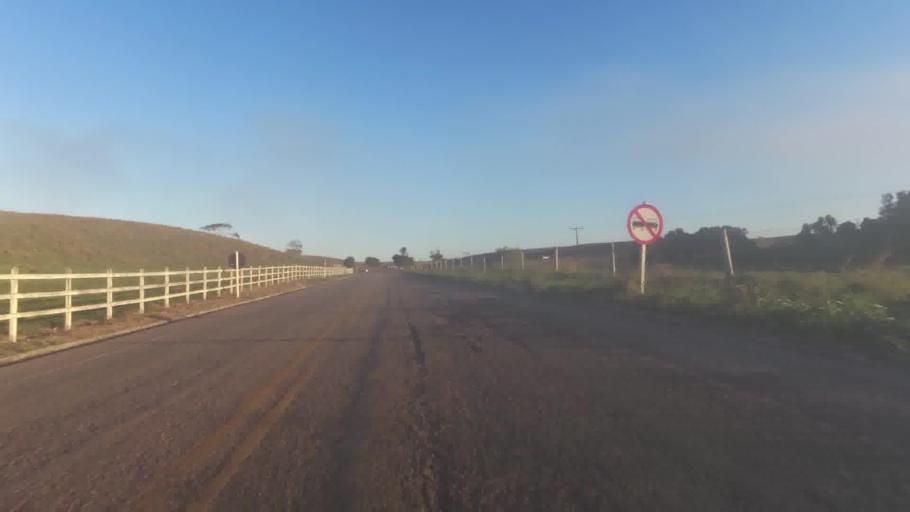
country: BR
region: Espirito Santo
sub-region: Marataizes
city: Marataizes
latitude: -21.1517
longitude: -40.9984
